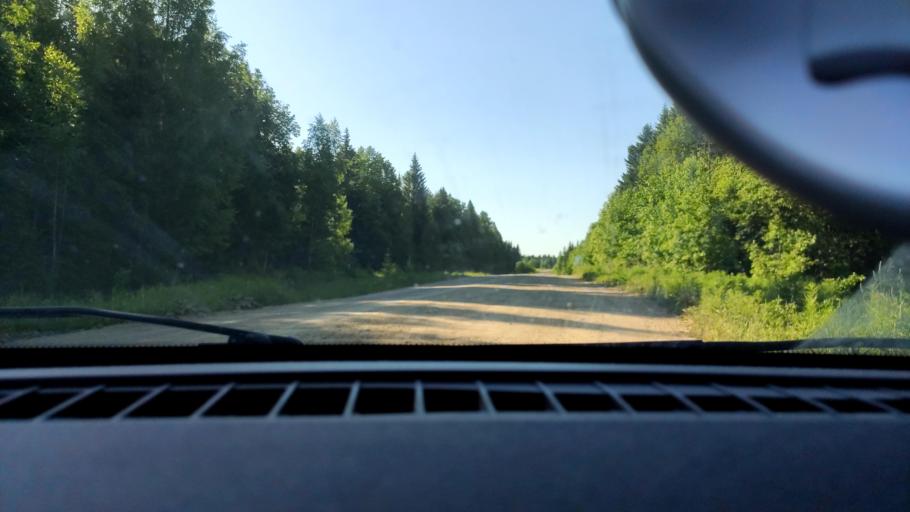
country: RU
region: Perm
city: Novyye Lyady
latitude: 58.1851
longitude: 56.5829
